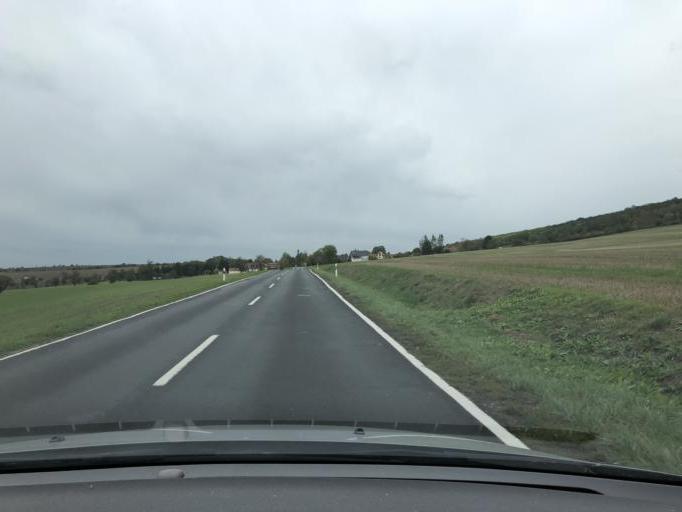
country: DE
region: Saxony-Anhalt
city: Eckartsberga
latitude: 51.1241
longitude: 11.5379
